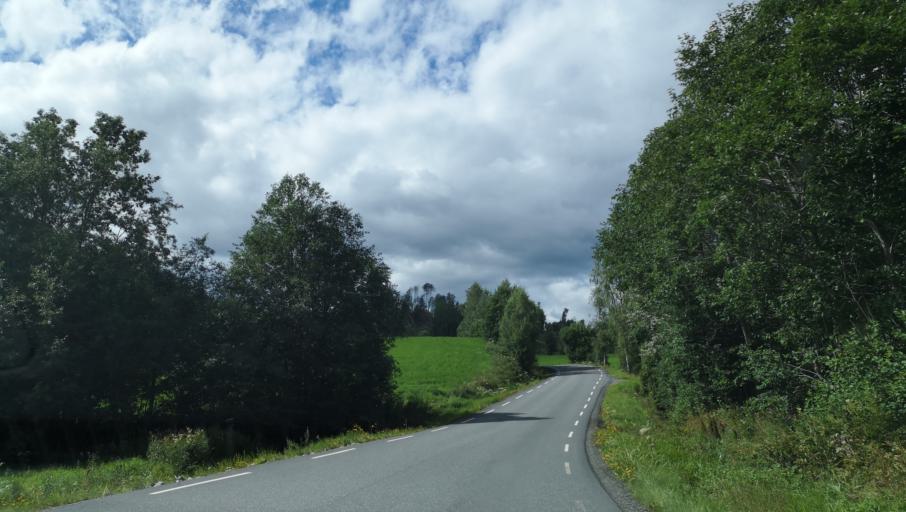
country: NO
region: Ostfold
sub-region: Hobol
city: Tomter
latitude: 59.6721
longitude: 10.9946
